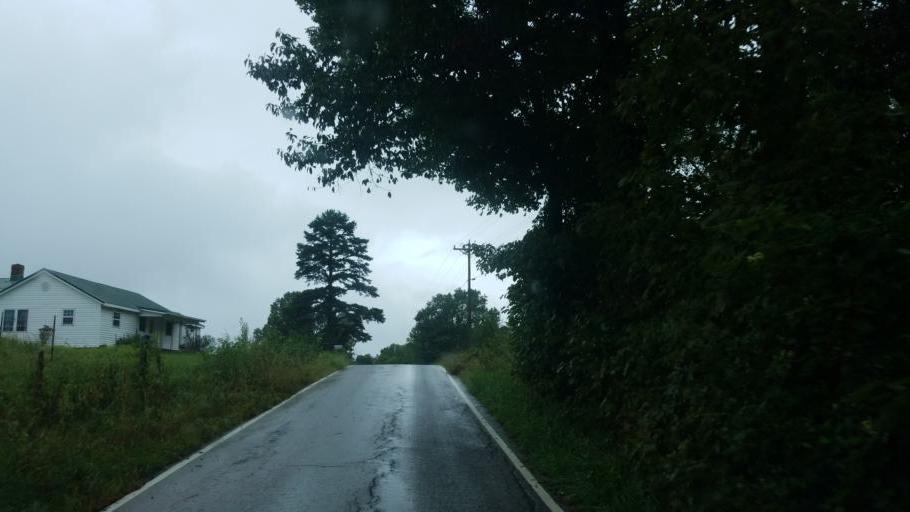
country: US
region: Kentucky
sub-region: Lewis County
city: Vanceburg
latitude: 38.4801
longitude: -83.5113
